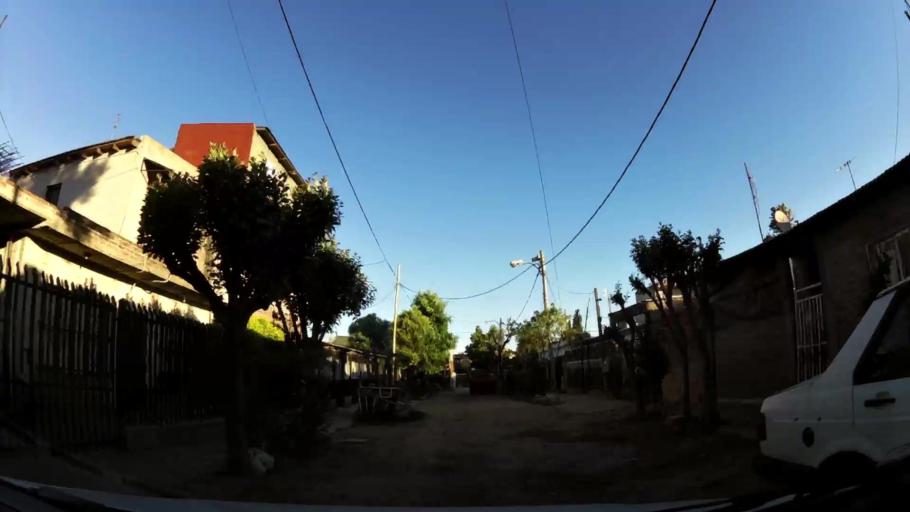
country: AR
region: Buenos Aires
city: San Justo
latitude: -34.7228
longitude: -58.6094
